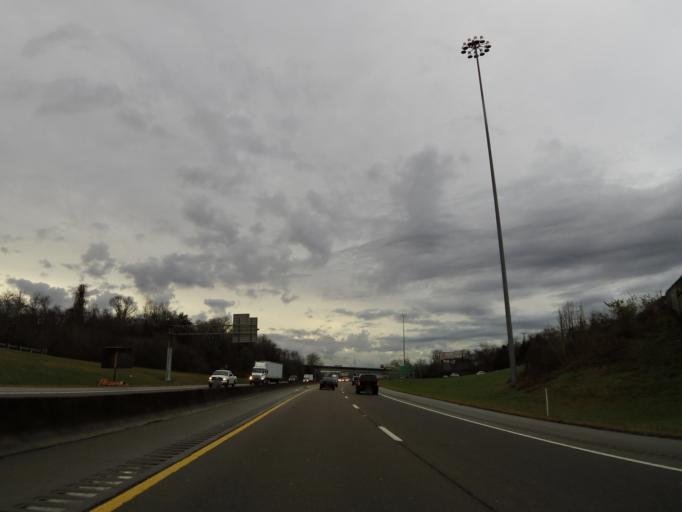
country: US
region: Tennessee
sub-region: Knox County
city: Knoxville
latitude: 36.0011
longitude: -83.9597
